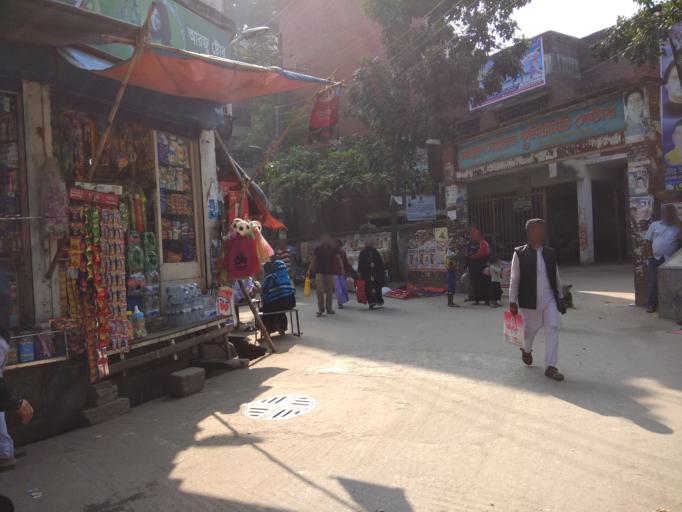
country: BD
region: Dhaka
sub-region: Dhaka
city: Dhaka
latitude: 23.7188
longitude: 90.4034
